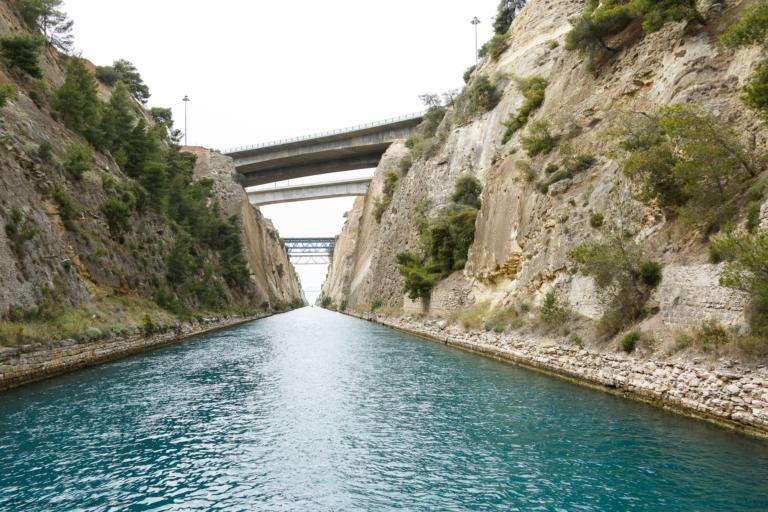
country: GR
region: Peloponnese
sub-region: Nomos Korinthias
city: Isthmia
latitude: 37.9236
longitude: 22.9995
